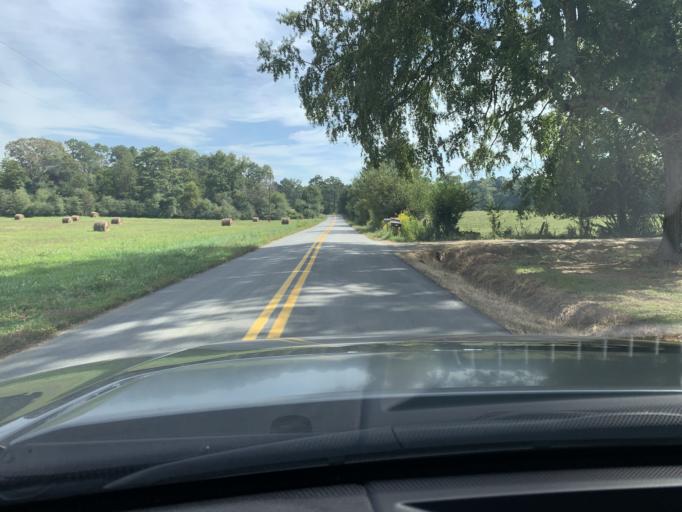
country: US
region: Georgia
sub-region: Polk County
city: Cedartown
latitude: 33.9476
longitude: -85.3755
